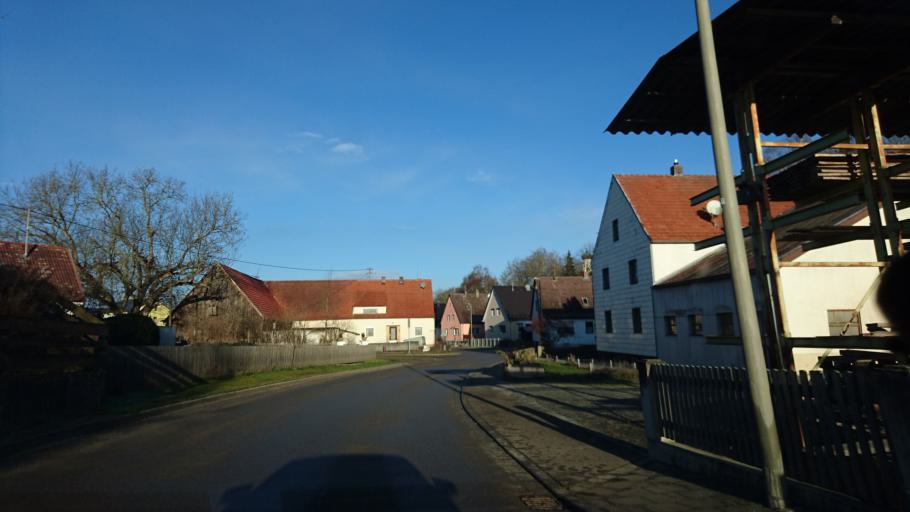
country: DE
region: Bavaria
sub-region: Swabia
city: Kuhlenthal
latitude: 48.5500
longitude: 10.7922
